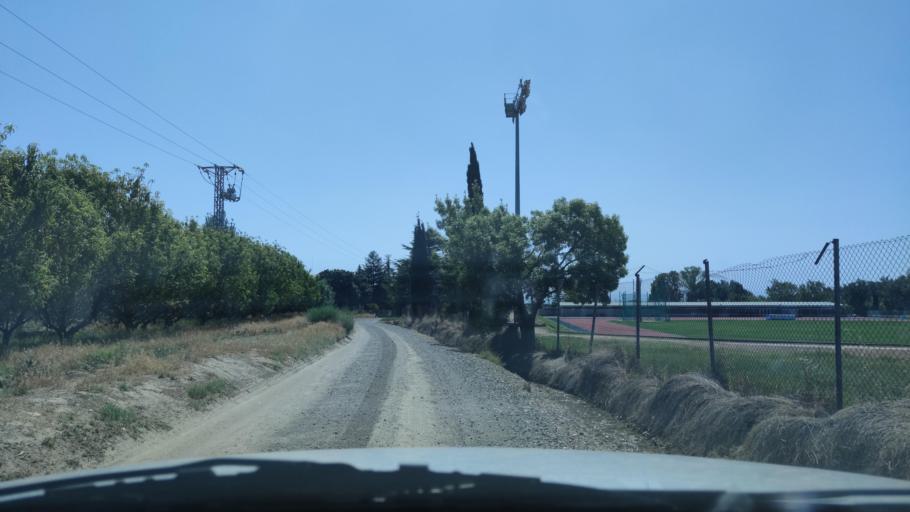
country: ES
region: Catalonia
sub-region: Provincia de Lleida
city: Alpicat
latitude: 41.6489
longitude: 0.5706
